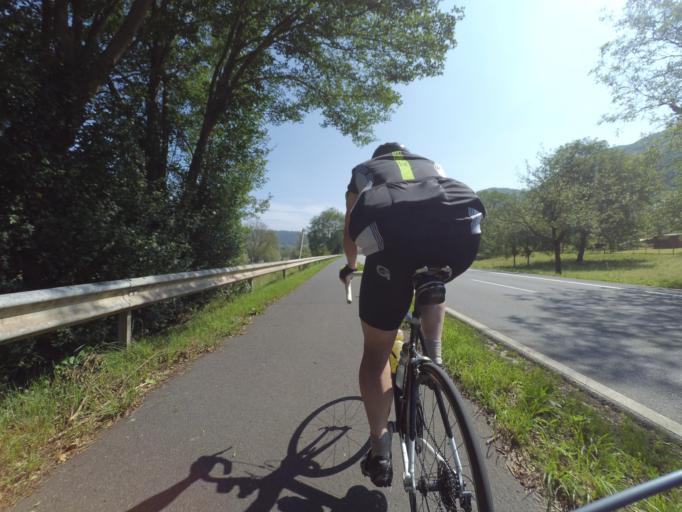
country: DE
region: Rheinland-Pfalz
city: Burgen
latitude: 50.2177
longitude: 7.3946
